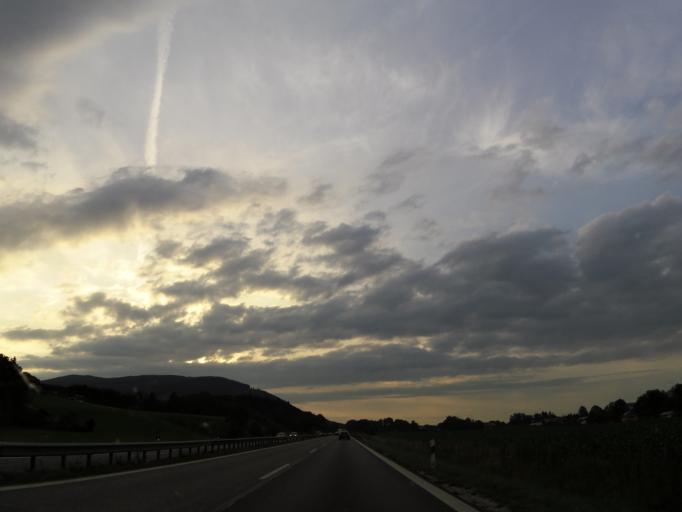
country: DE
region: Bavaria
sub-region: Upper Bavaria
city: Anger
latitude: 47.7979
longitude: 12.8583
